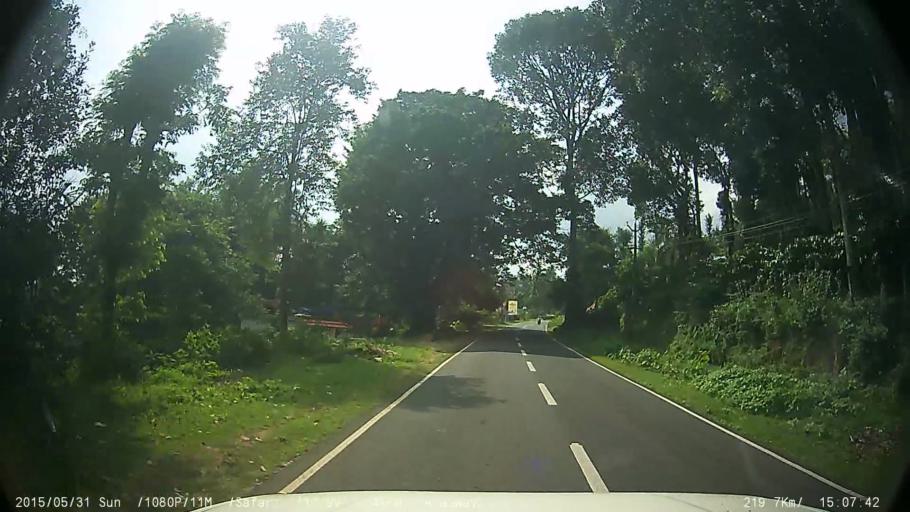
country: IN
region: Kerala
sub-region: Wayanad
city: Kalpetta
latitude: 11.6480
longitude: 76.2182
